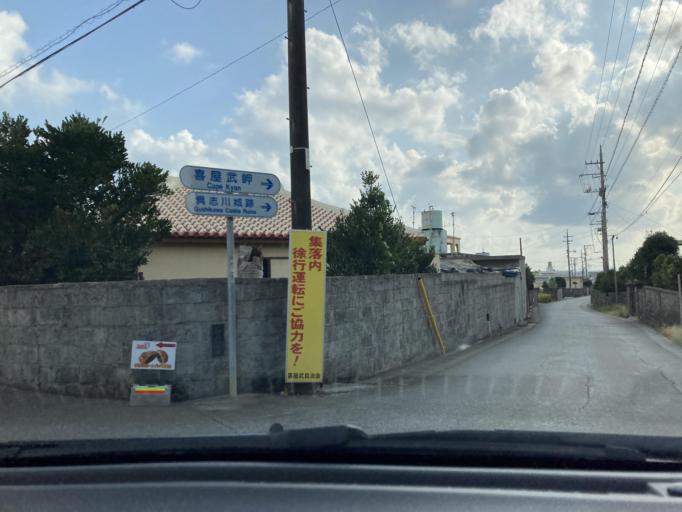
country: JP
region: Okinawa
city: Itoman
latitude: 26.0920
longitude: 127.6634
